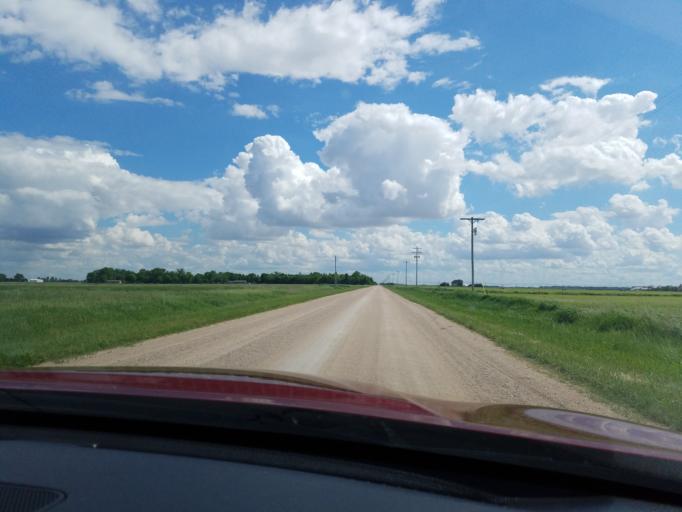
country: US
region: Nebraska
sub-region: Buffalo County
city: Kearney
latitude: 40.6514
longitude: -99.0085
